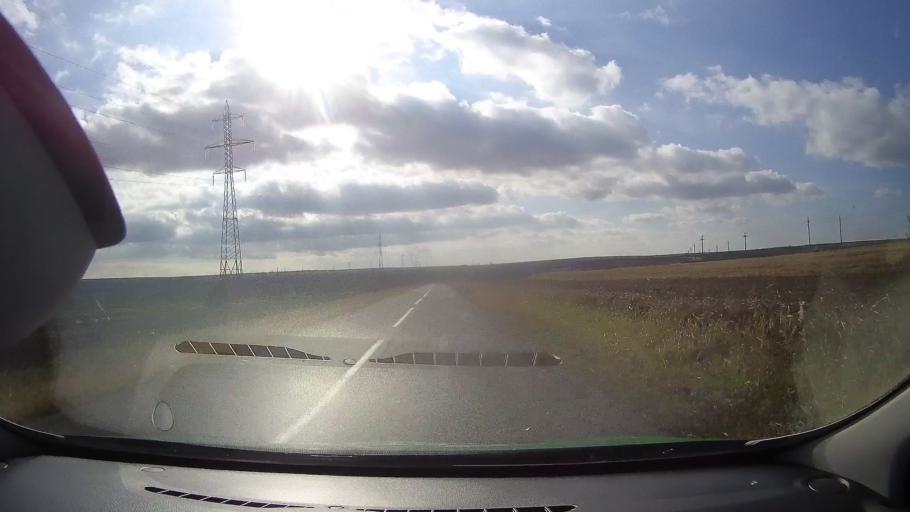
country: RO
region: Constanta
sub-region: Comuna Sacele
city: Sacele
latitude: 44.5021
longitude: 28.6625
